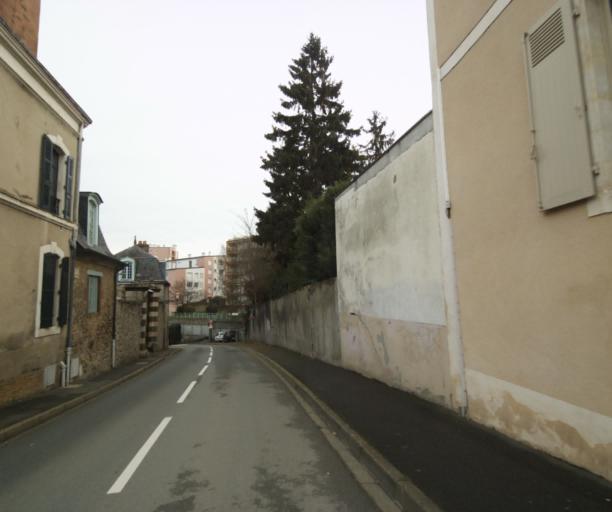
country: FR
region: Pays de la Loire
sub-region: Departement de la Sarthe
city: Coulaines
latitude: 48.0136
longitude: 0.2034
